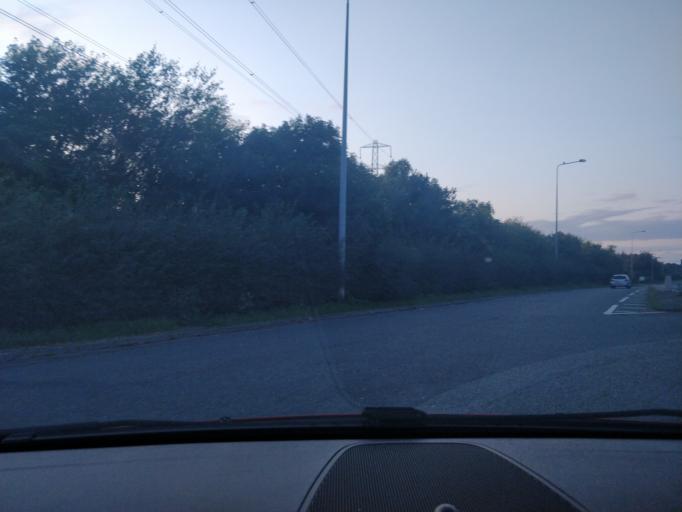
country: GB
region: England
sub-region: Lancashire
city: Tarleton
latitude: 53.6863
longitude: -2.8161
